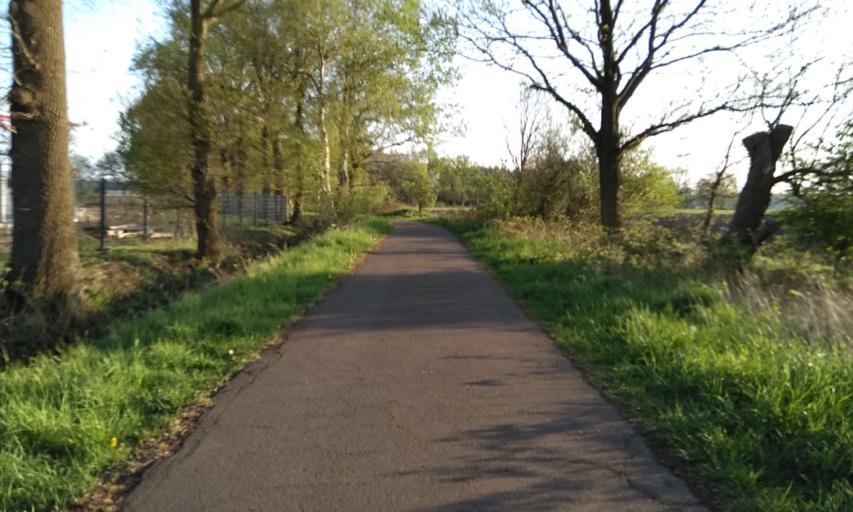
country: DE
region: Lower Saxony
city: Dollern
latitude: 53.5322
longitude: 9.5450
